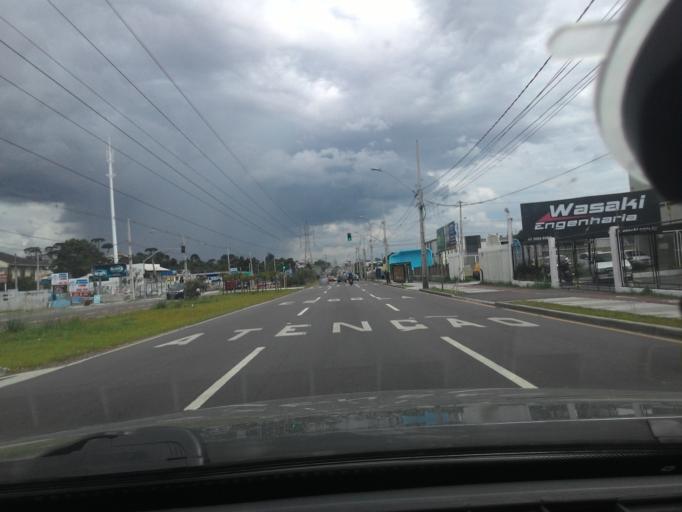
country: BR
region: Parana
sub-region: Pinhais
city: Pinhais
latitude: -25.4772
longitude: -49.2257
